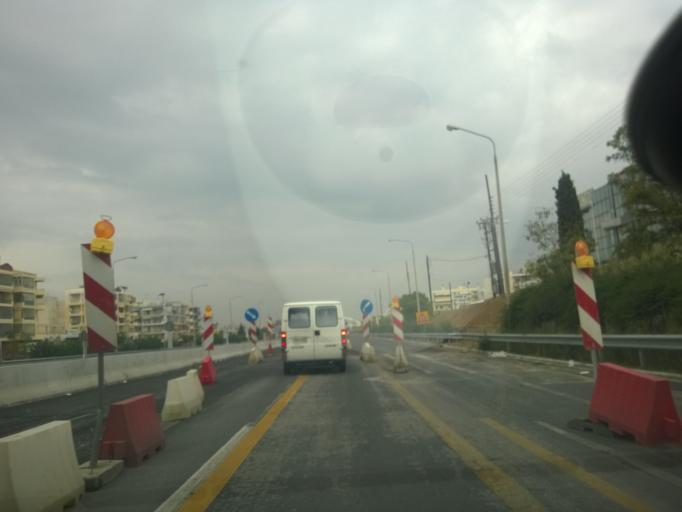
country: GR
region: Central Macedonia
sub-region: Nomos Thessalonikis
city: Evosmos
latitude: 40.6777
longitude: 22.9152
